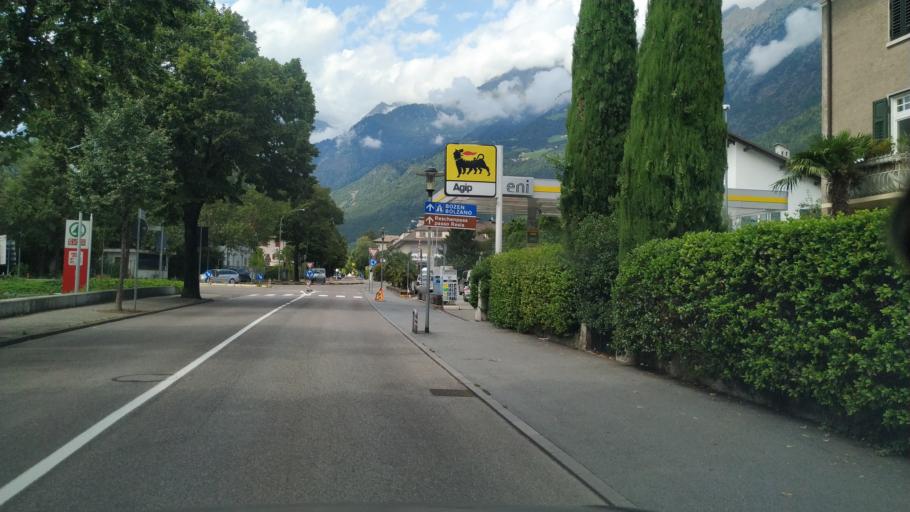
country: IT
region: Trentino-Alto Adige
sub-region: Bolzano
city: Merano
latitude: 46.6767
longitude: 11.1496
